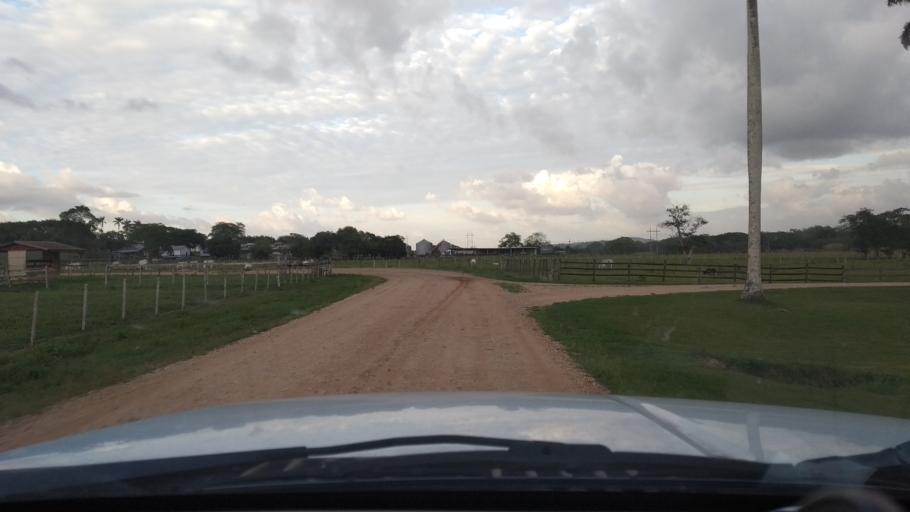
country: BZ
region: Cayo
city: San Ignacio
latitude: 17.2242
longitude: -88.9933
